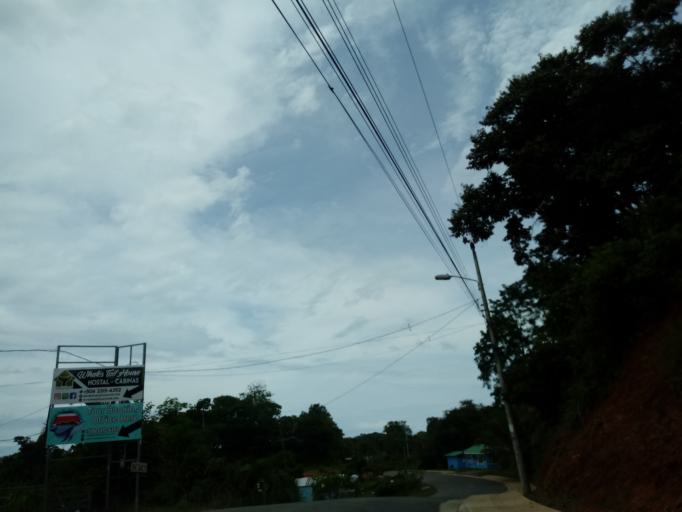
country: CR
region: San Jose
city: Mercedes
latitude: 9.1611
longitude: -83.7363
